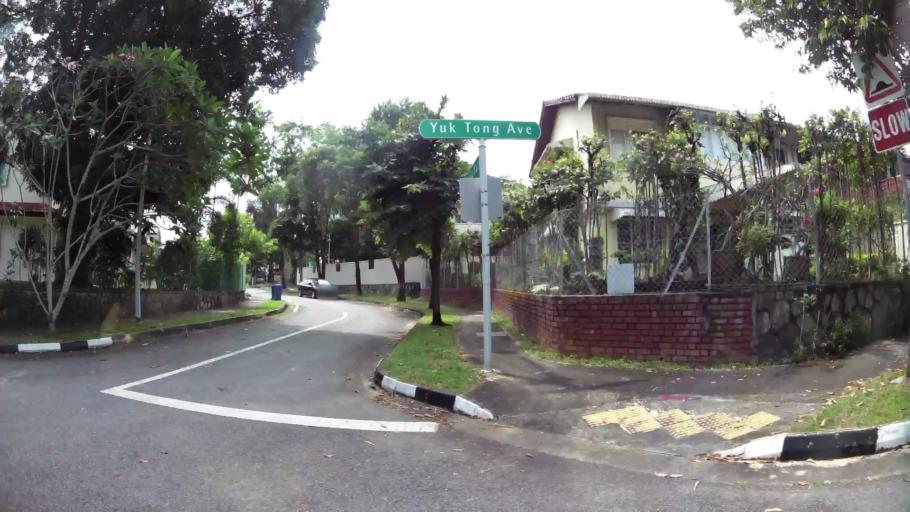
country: SG
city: Singapore
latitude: 1.3446
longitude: 103.7731
